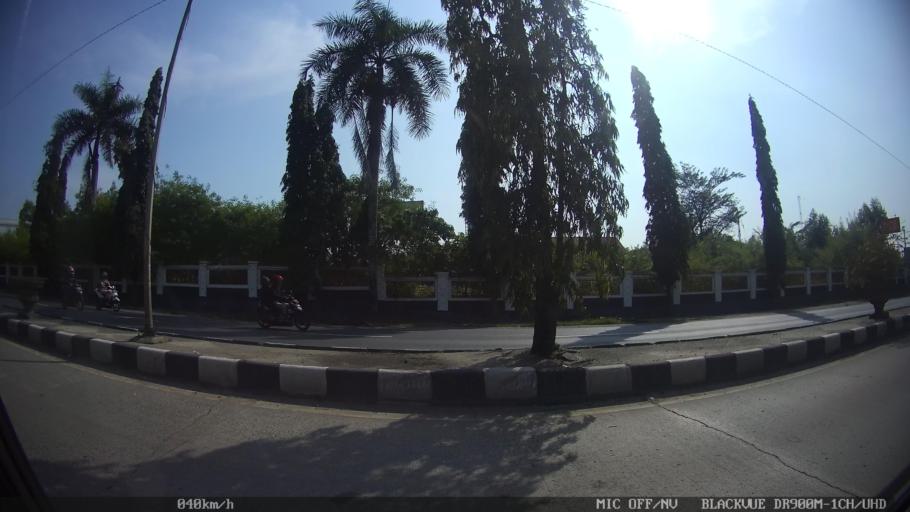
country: ID
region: Lampung
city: Natar
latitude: -5.2447
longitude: 105.1771
